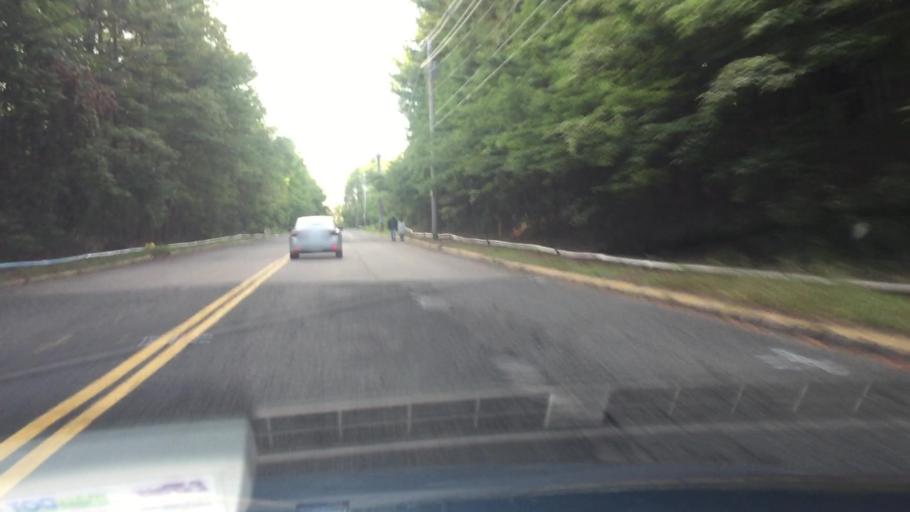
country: US
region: Massachusetts
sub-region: Worcester County
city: Northborough
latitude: 42.3313
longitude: -71.6005
